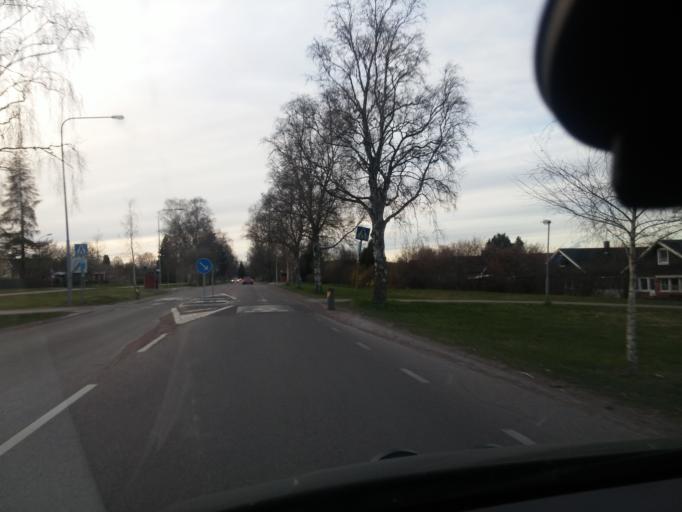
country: SE
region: Dalarna
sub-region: Borlange Kommun
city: Borlaenge
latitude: 60.5085
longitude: 15.4228
